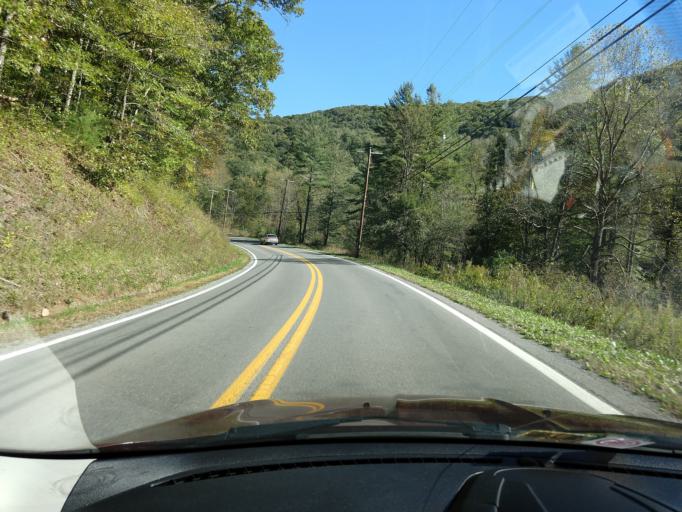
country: US
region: West Virginia
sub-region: Pocahontas County
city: Marlinton
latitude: 38.2094
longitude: -80.0522
